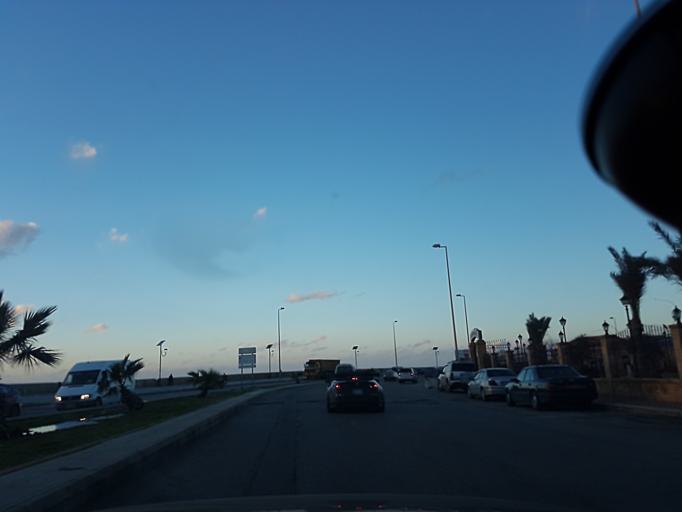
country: LB
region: Liban-Sud
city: Sidon
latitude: 33.5617
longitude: 35.3672
